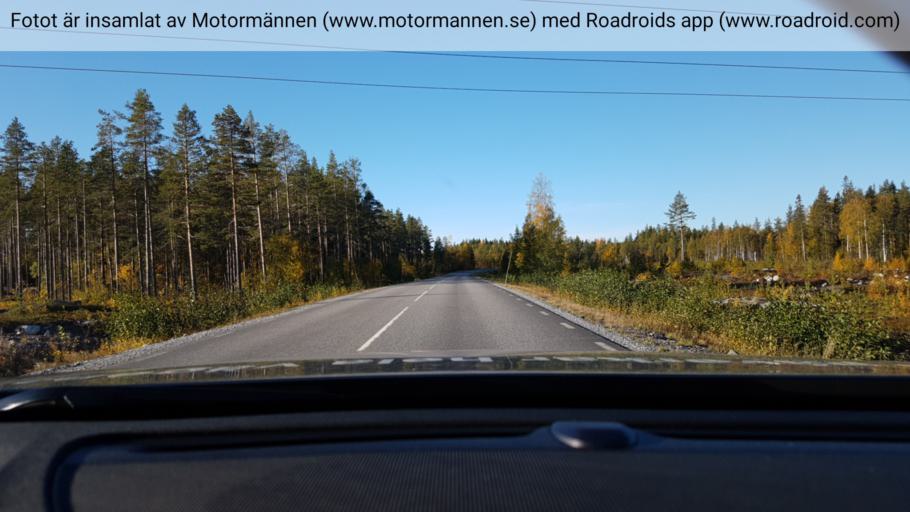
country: SE
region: Norrbotten
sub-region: Pitea Kommun
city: Roknas
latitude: 65.3464
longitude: 21.0091
